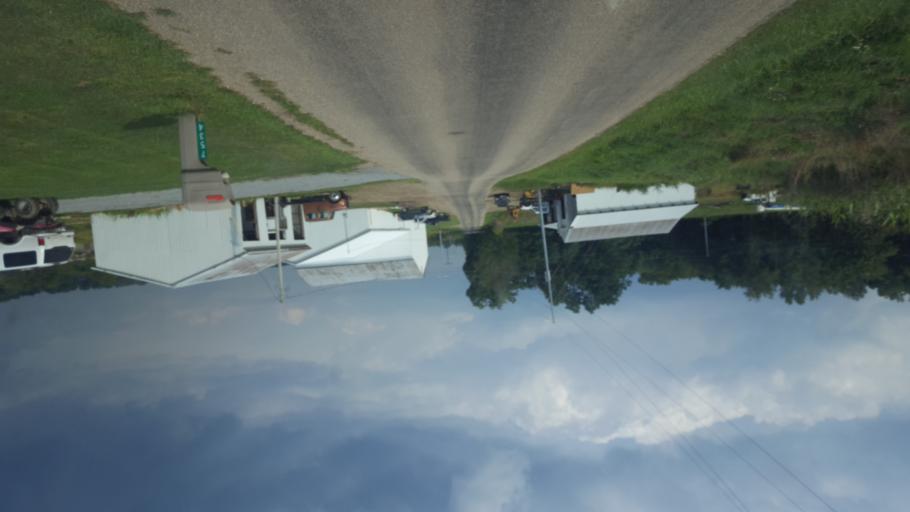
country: US
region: Ohio
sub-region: Knox County
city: Gambier
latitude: 40.3389
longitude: -82.3882
